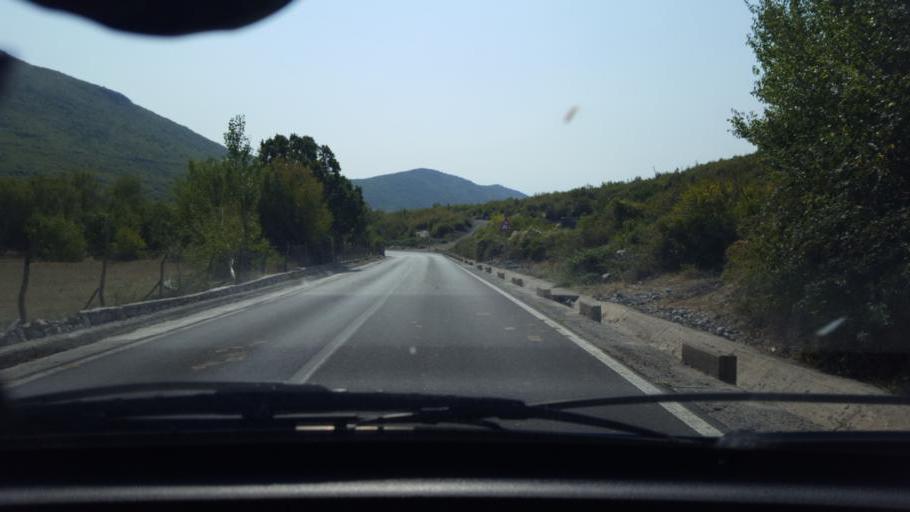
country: AL
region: Shkoder
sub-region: Rrethi i Malesia e Madhe
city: Kastrat
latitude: 42.3860
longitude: 19.4926
